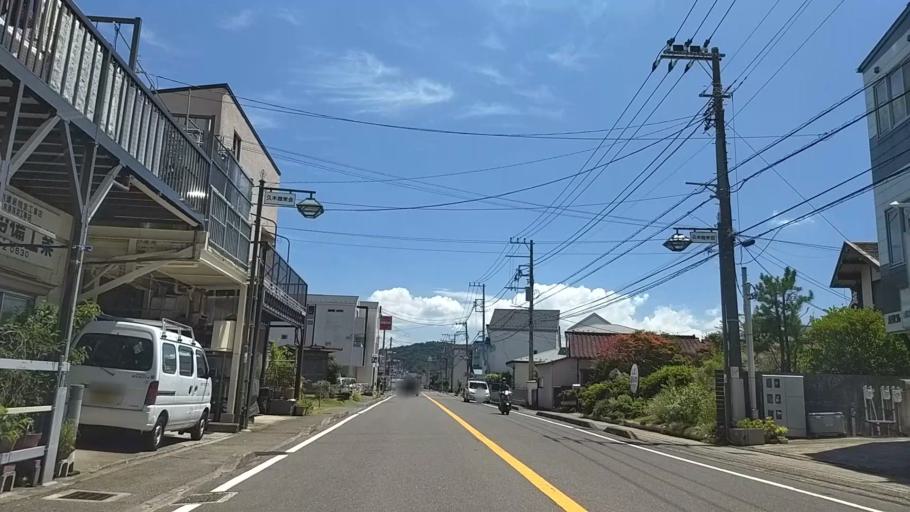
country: JP
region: Kanagawa
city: Zushi
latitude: 35.3025
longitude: 139.5700
